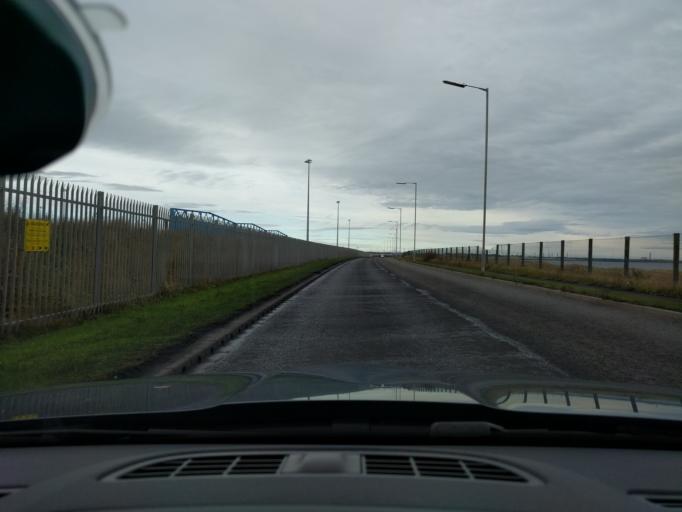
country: GB
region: England
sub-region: Northumberland
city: Blyth
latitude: 55.1382
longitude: -1.5128
